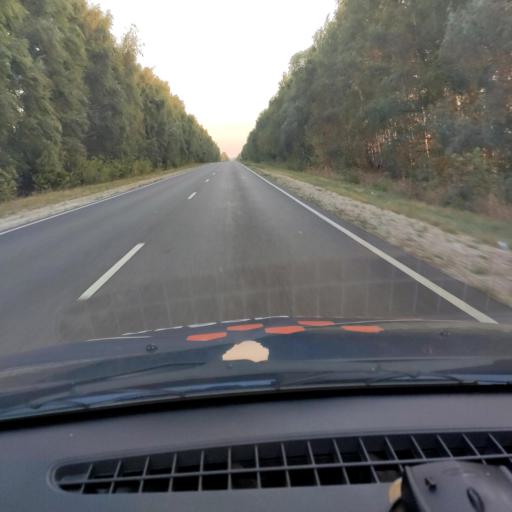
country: RU
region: Voronezj
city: Latnaya
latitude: 51.6427
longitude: 38.7868
